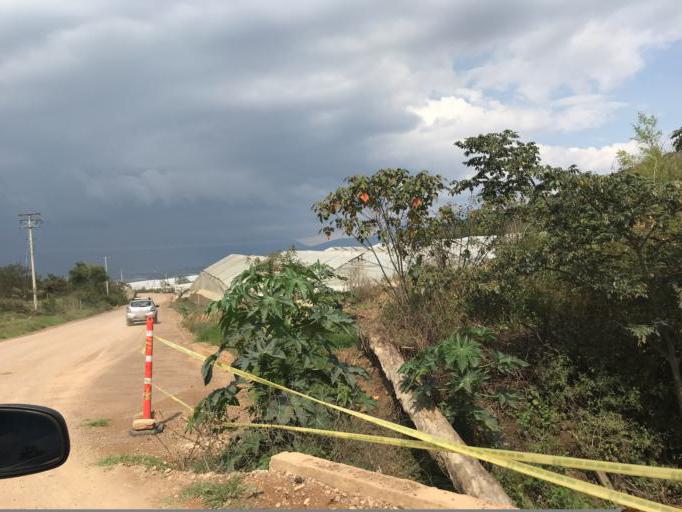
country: CO
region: Boyaca
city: Villa de Leiva
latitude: 5.6503
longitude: -73.5909
